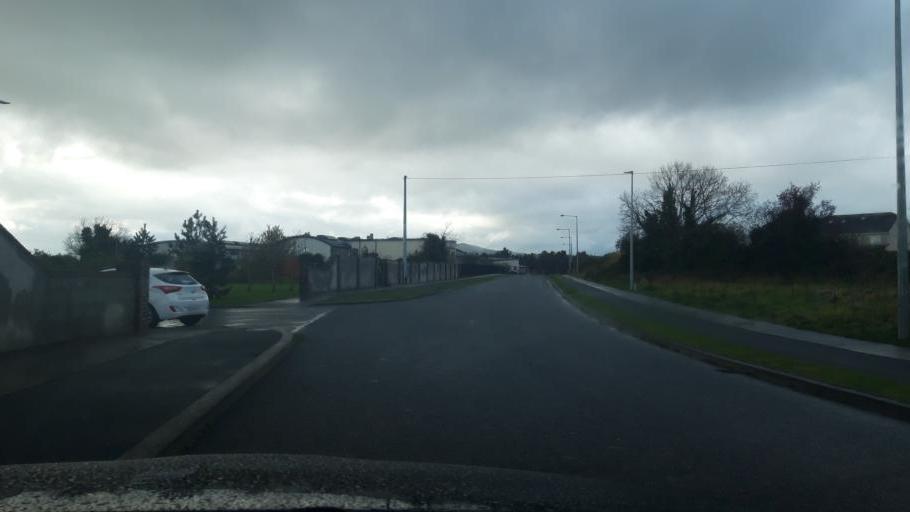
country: IE
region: Leinster
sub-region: Wicklow
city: Kilcoole
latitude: 53.1019
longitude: -6.0595
